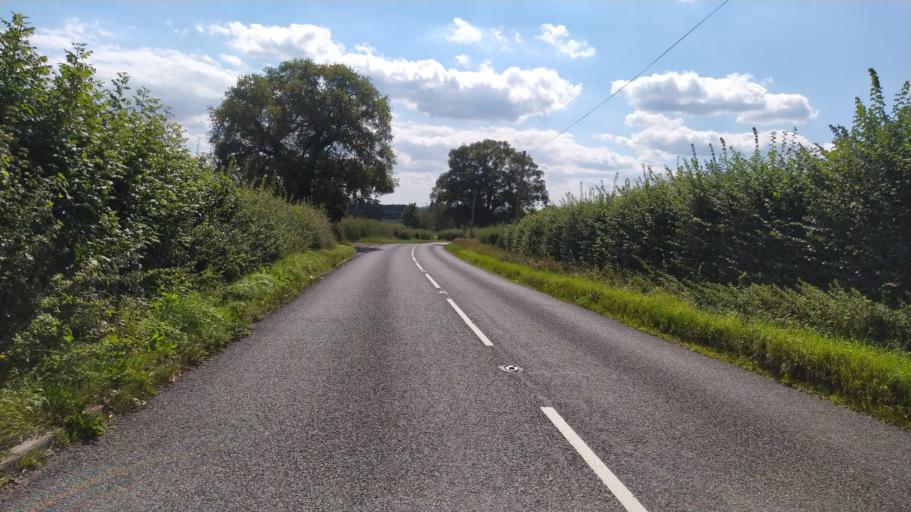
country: GB
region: England
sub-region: Wiltshire
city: Mere
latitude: 51.0871
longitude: -2.2817
